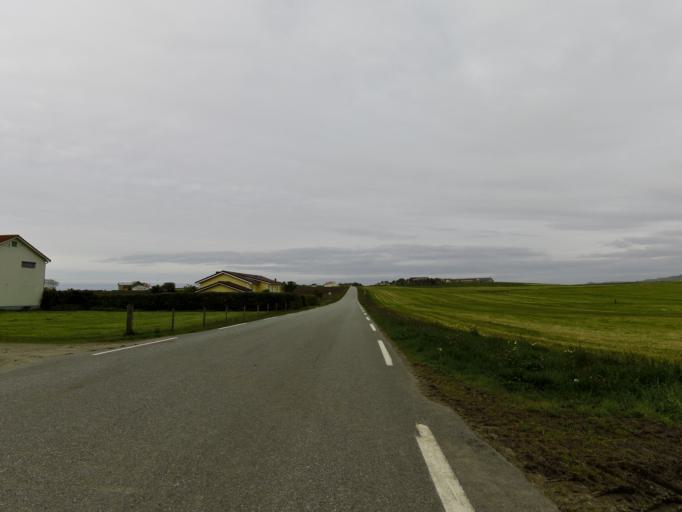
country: NO
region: Rogaland
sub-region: Klepp
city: Kleppe
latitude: 58.8148
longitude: 5.5785
